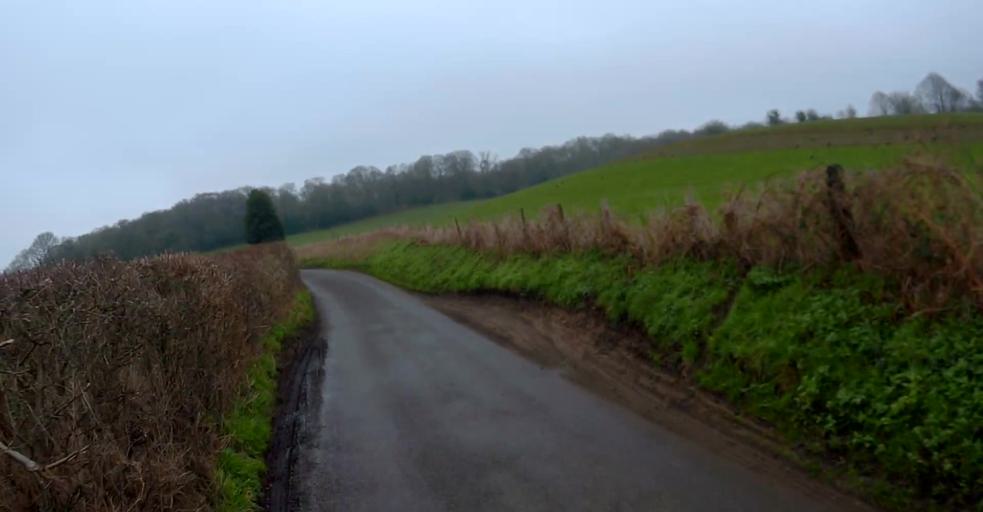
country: GB
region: England
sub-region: Hampshire
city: Hook
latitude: 51.3203
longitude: -0.9351
